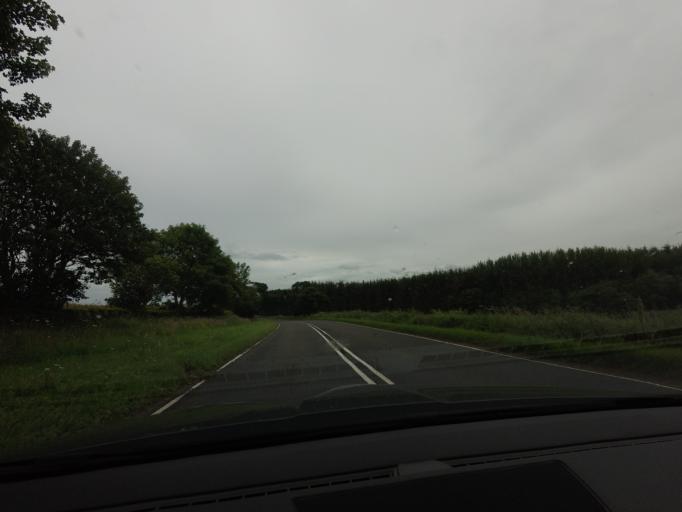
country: GB
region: Scotland
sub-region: Moray
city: Cullen
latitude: 57.6781
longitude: -2.7689
